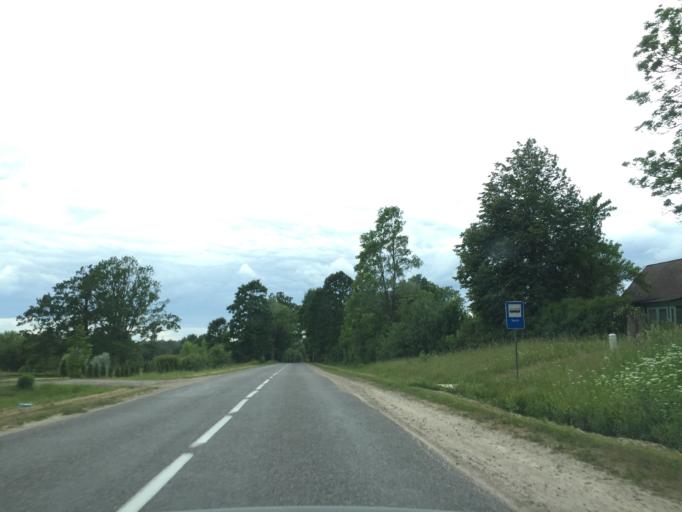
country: LV
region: Vilanu
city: Vilani
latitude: 56.4434
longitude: 27.0942
